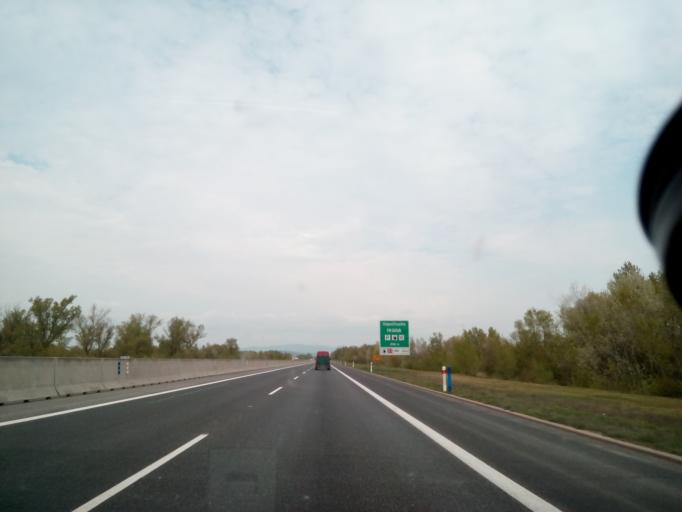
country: SK
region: Trenciansky
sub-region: Okres Nove Mesto nad Vahom
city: Nove Mesto nad Vahom
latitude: 48.6824
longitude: 17.8727
